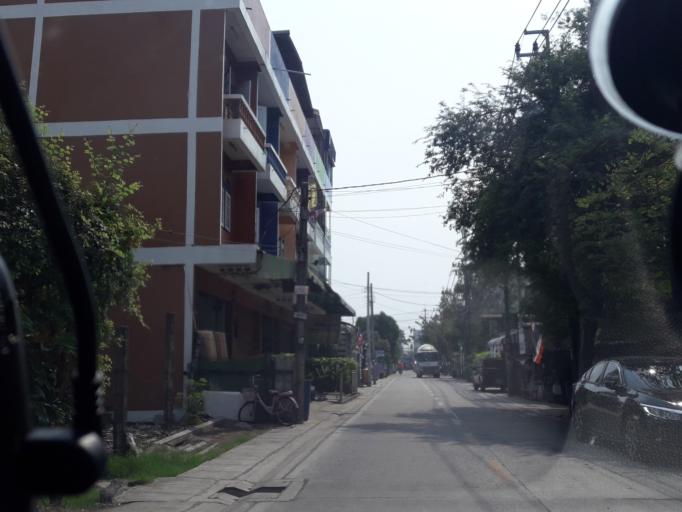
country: TH
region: Bangkok
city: Min Buri
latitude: 13.8151
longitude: 100.7055
